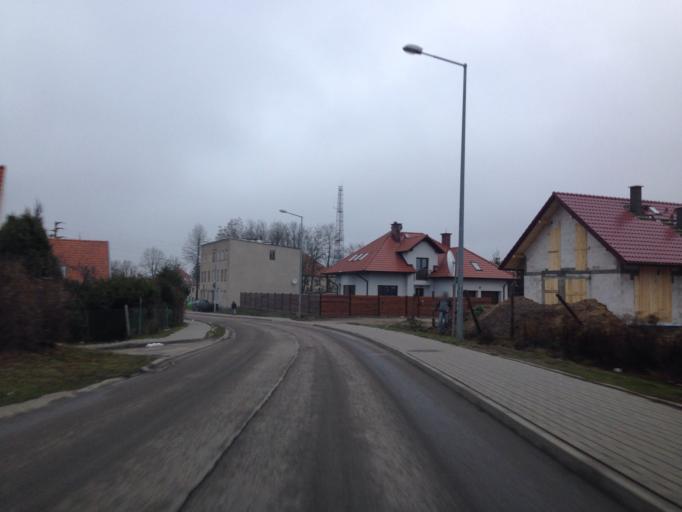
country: PL
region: Warmian-Masurian Voivodeship
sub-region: Powiat ketrzynski
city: Ketrzyn
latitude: 54.0663
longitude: 21.3788
